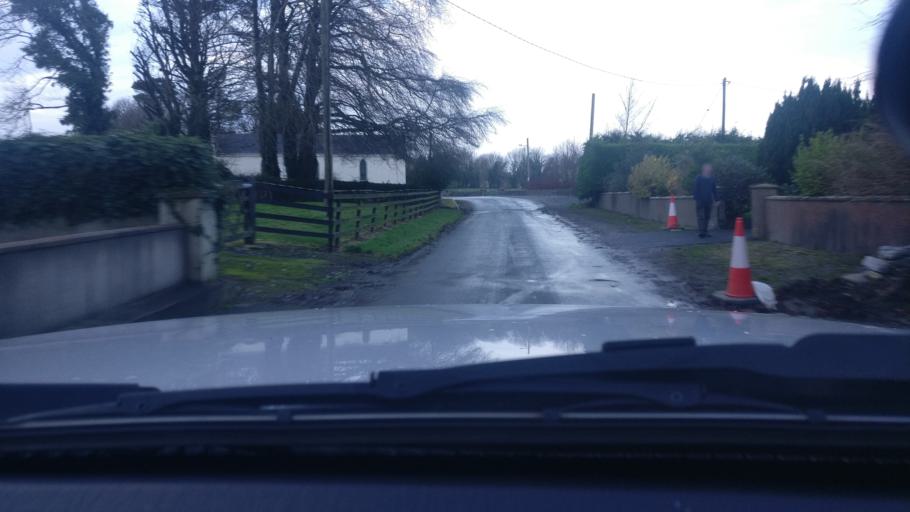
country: IE
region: Connaught
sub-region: County Galway
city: Loughrea
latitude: 53.1623
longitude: -8.5215
